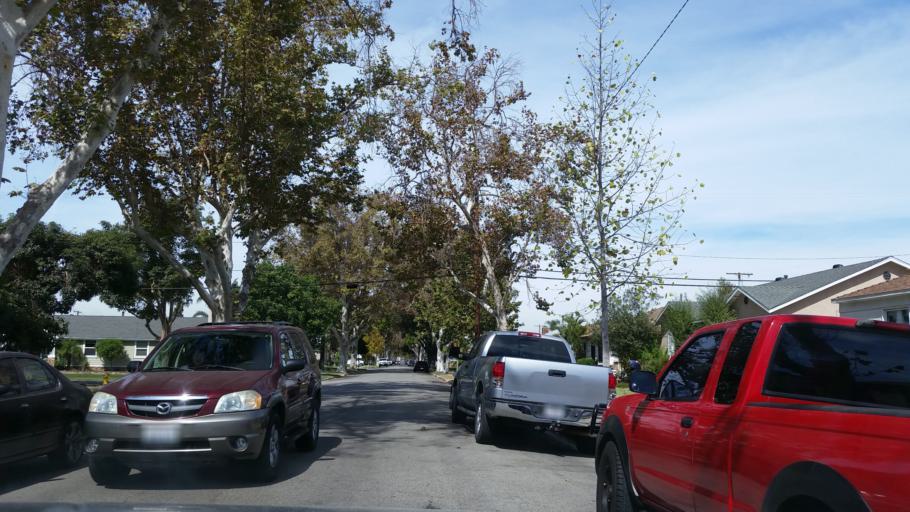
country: US
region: California
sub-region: Los Angeles County
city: Lakewood
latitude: 33.8614
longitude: -118.1401
